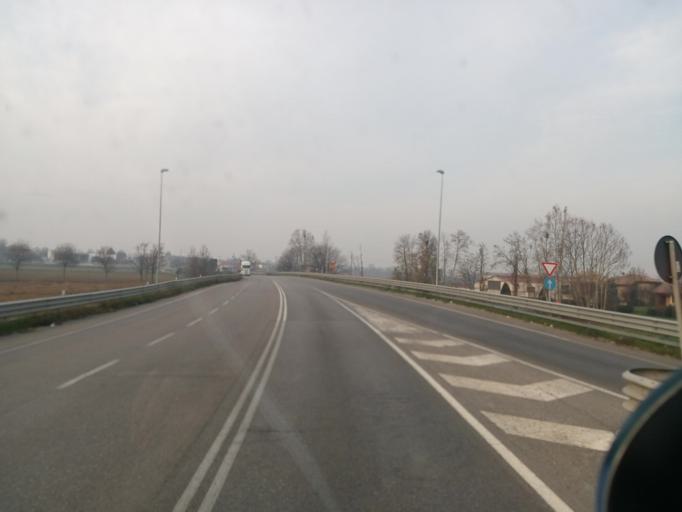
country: IT
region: Lombardy
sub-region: Provincia di Brescia
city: Vighizzolo
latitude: 45.4228
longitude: 10.3722
